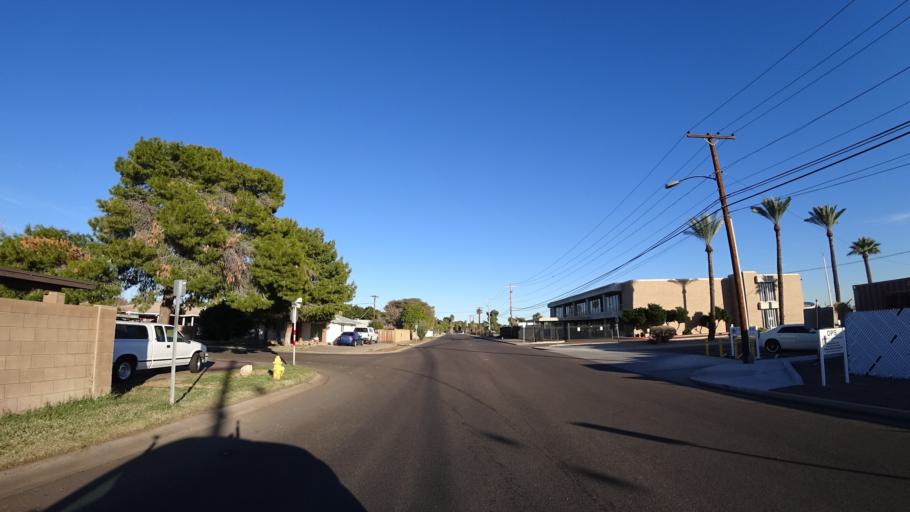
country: US
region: Arizona
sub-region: Maricopa County
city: Phoenix
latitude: 33.4750
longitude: -112.1027
